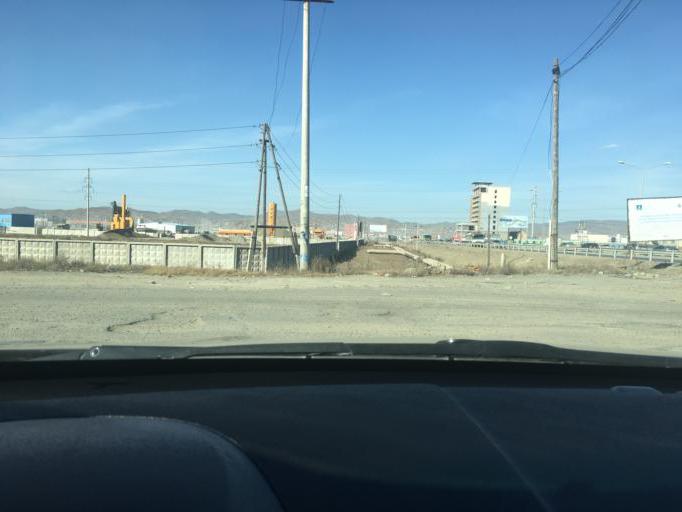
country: MN
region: Ulaanbaatar
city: Ulaanbaatar
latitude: 47.8882
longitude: 106.7848
